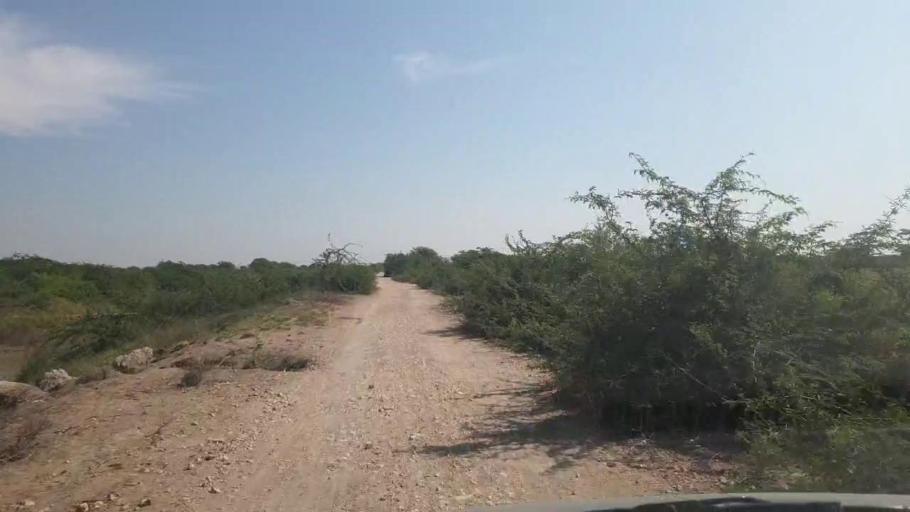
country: PK
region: Sindh
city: Digri
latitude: 24.9540
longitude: 69.1417
